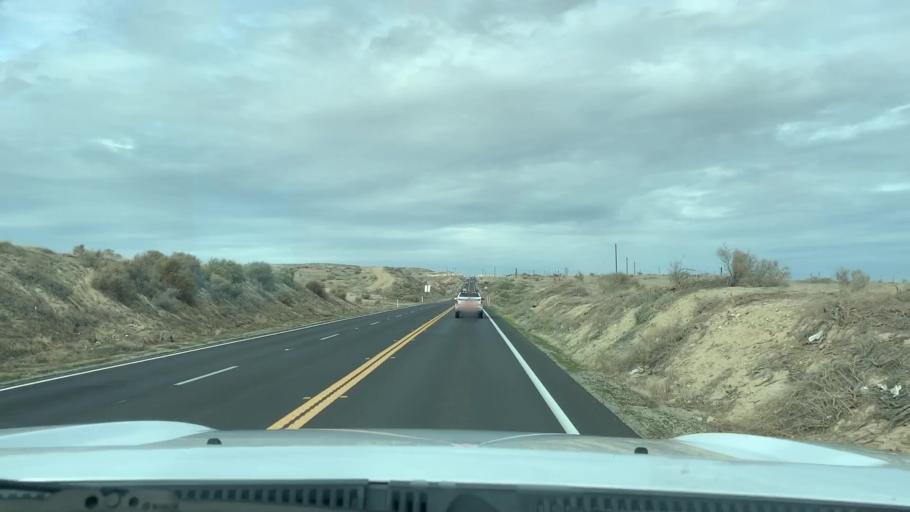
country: US
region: California
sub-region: Kern County
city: South Taft
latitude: 35.1089
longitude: -119.4234
